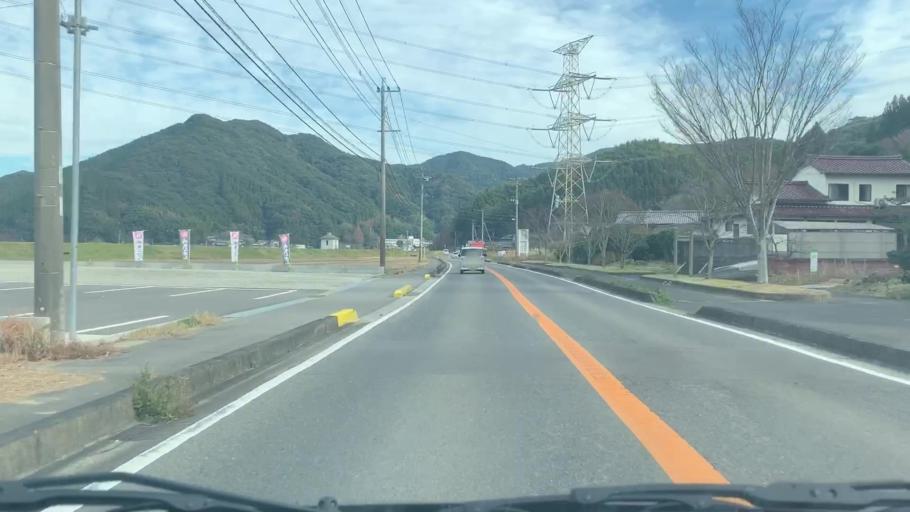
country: JP
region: Saga Prefecture
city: Karatsu
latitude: 33.3567
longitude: 130.0057
